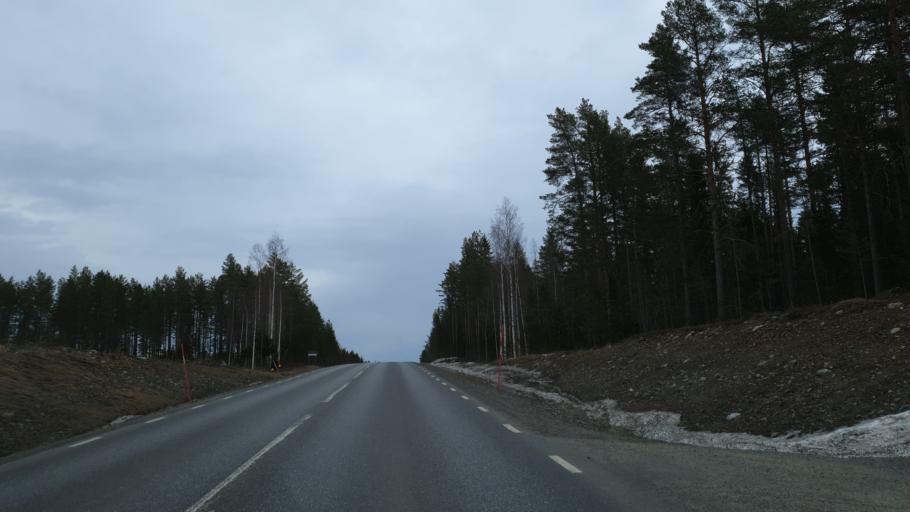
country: SE
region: Vaesterbotten
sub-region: Robertsfors Kommun
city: Robertsfors
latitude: 64.2202
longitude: 20.9085
